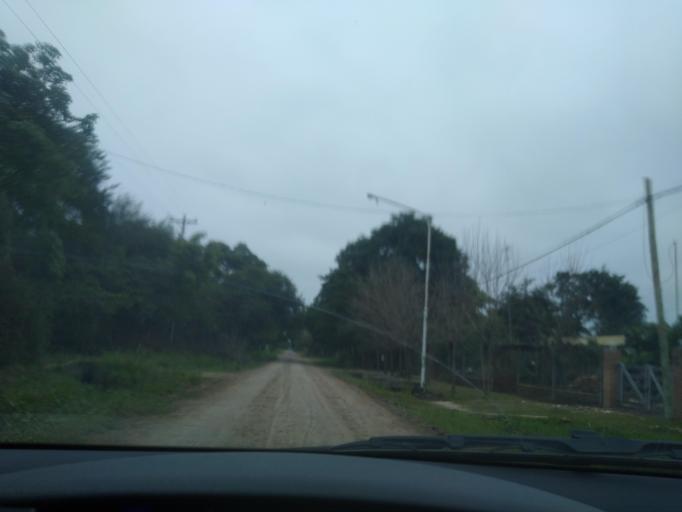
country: AR
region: Chaco
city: Colonia Benitez
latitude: -27.3322
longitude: -58.9614
